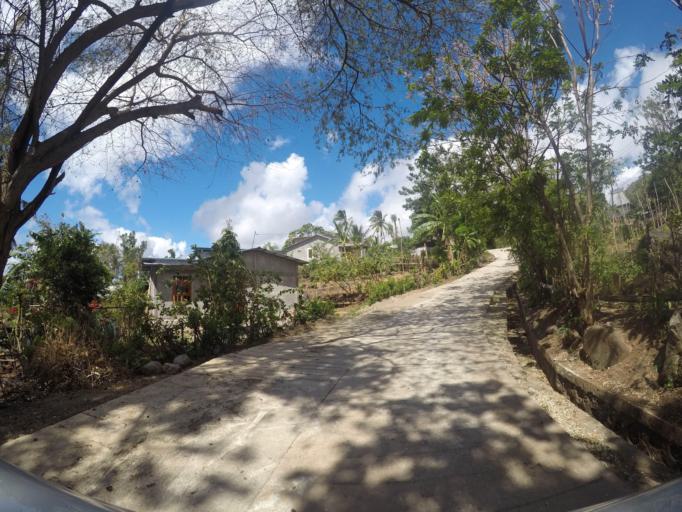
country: TL
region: Lautem
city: Lospalos
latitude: -8.5365
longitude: 126.7998
